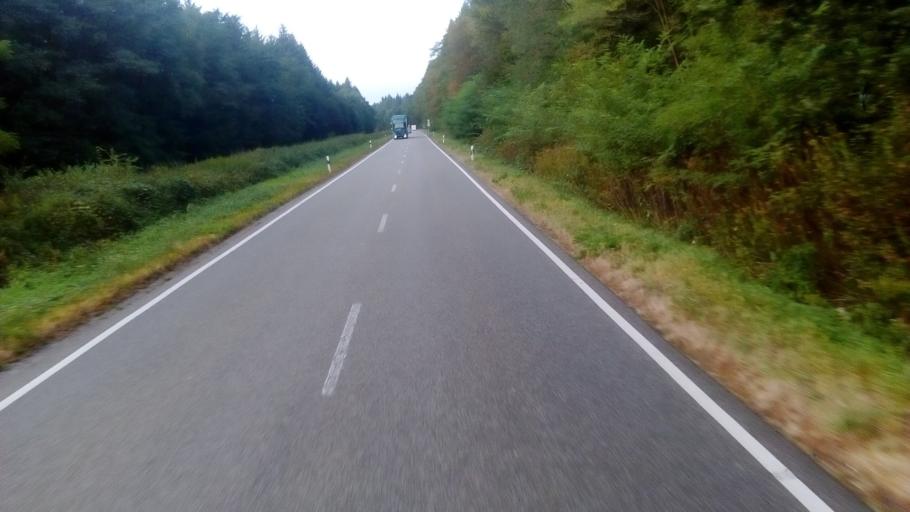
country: DE
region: Rheinland-Pfalz
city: Berg
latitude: 49.0161
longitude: 8.1900
